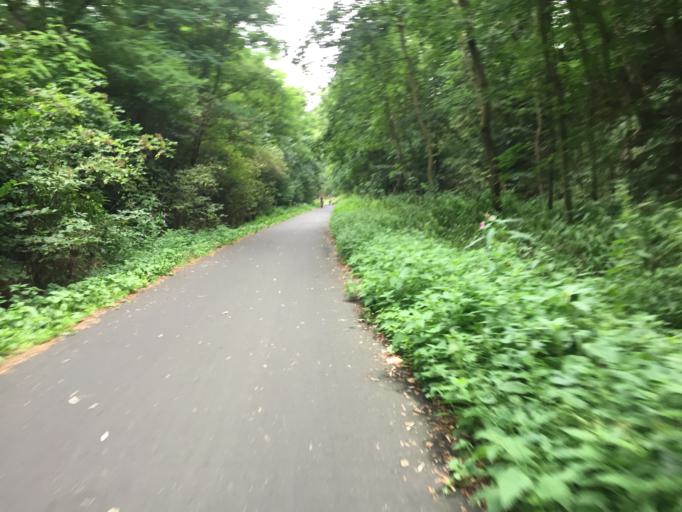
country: DE
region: Hesse
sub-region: Regierungsbezirk Kassel
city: Bad Hersfeld
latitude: 50.8854
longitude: 9.7323
